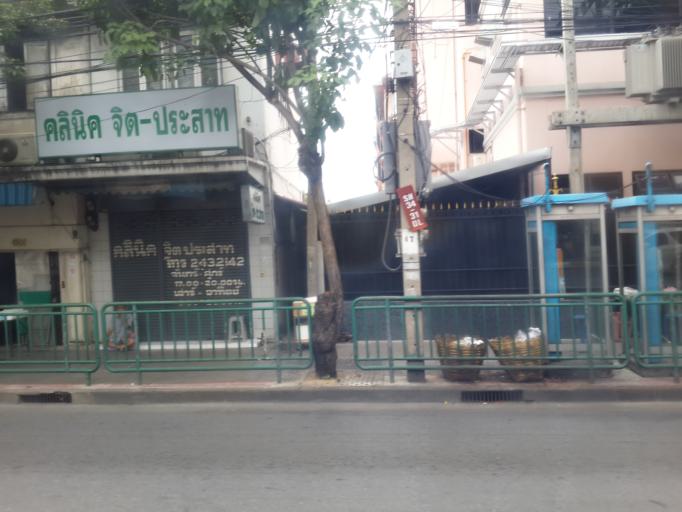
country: TH
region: Bangkok
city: Phra Nakhon
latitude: 13.7752
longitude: 100.5068
